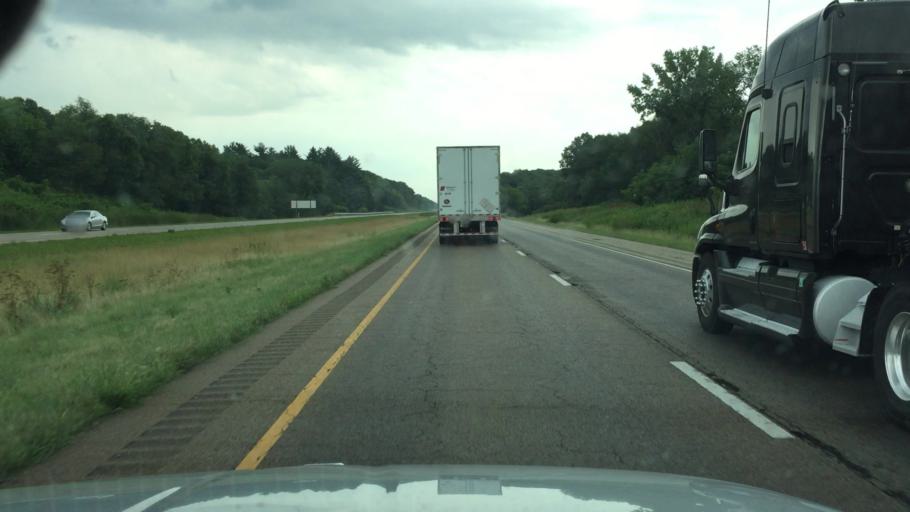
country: US
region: Illinois
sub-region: Peoria County
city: Bellevue
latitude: 40.7636
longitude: -89.7268
